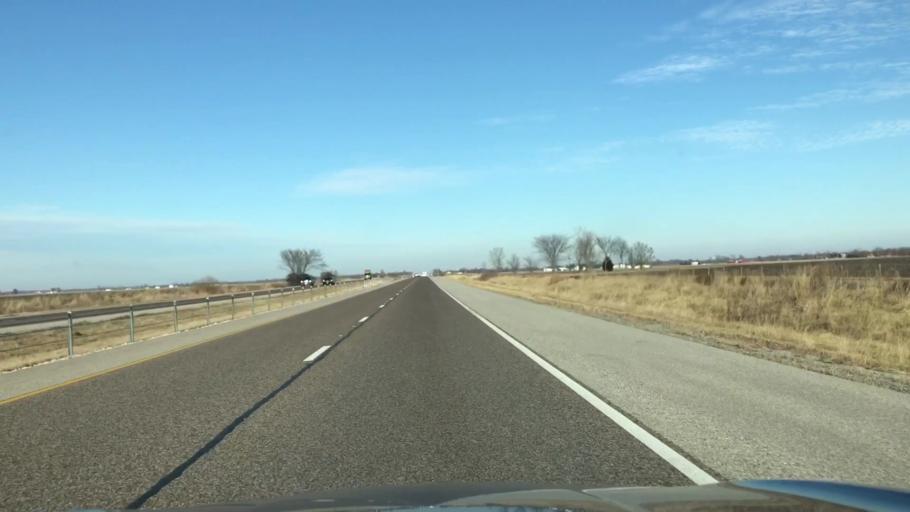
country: US
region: Illinois
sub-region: Madison County
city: Edwardsville
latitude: 38.8369
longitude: -89.8745
